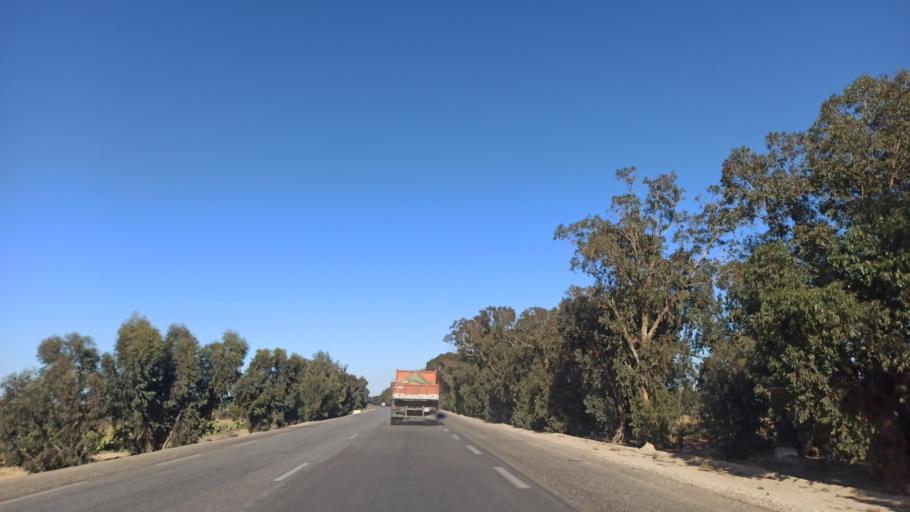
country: TN
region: Sidi Bu Zayd
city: Jilma
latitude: 35.1751
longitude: 9.3718
